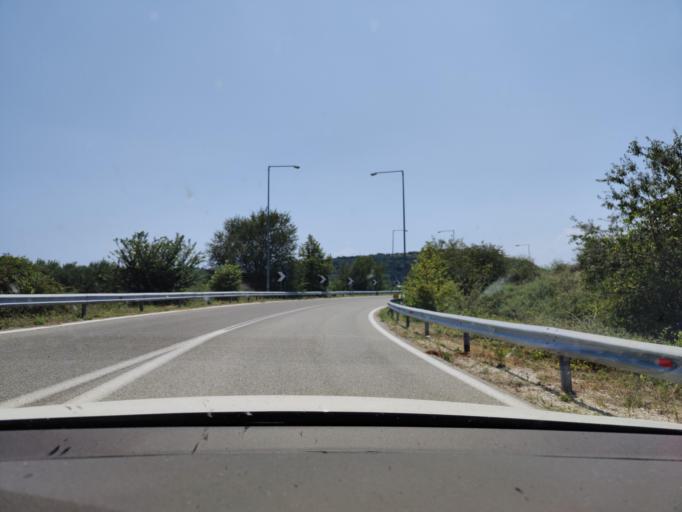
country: GR
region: East Macedonia and Thrace
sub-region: Nomos Kavalas
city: Paralia Ofryniou
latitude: 40.7844
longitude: 23.9588
